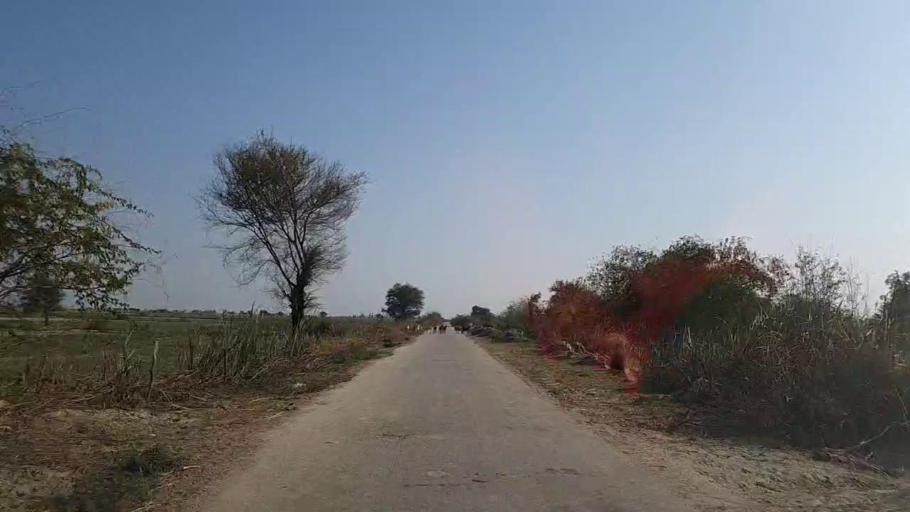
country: PK
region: Sindh
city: Sanghar
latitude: 25.9470
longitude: 69.0499
